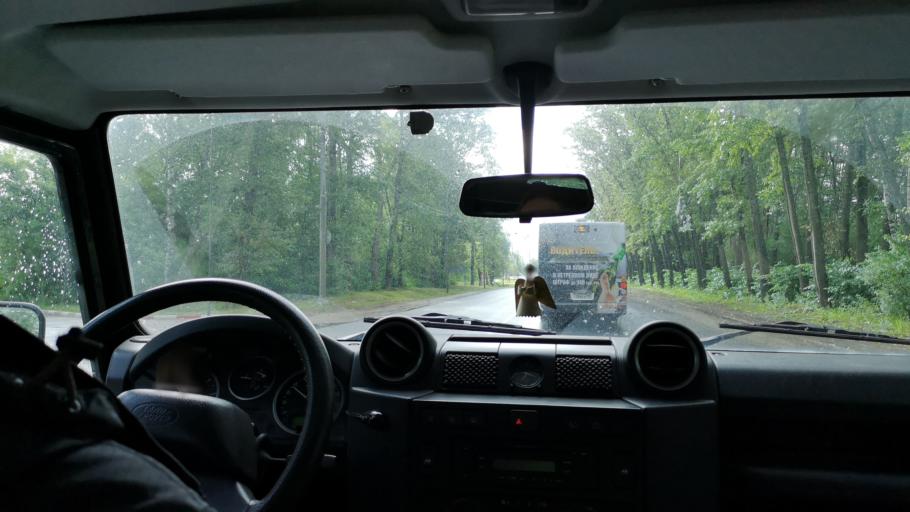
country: RU
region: Moskovskaya
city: Gorshkovo
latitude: 56.3670
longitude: 37.4633
